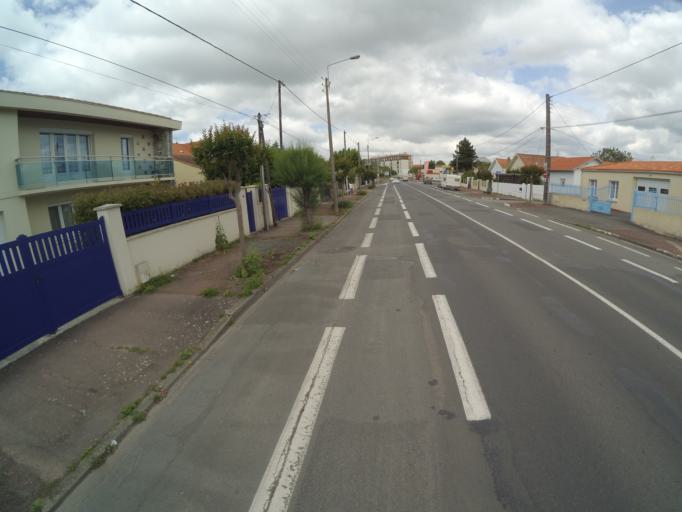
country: FR
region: Poitou-Charentes
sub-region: Departement de la Charente-Maritime
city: Rochefort
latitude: 45.9287
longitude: -0.9601
